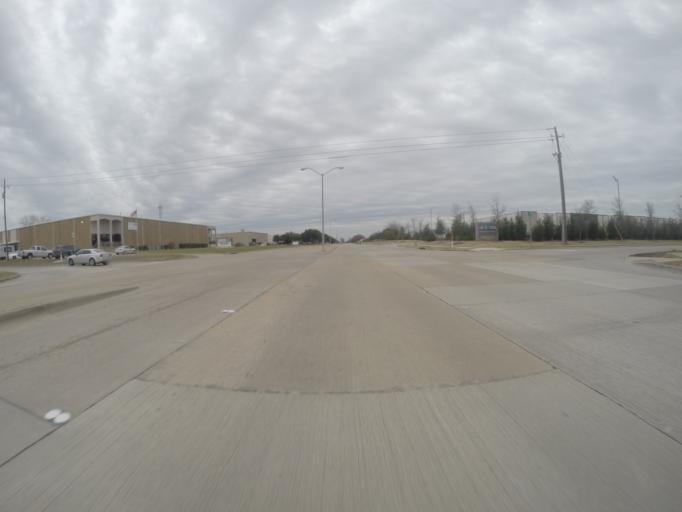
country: US
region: Texas
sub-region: Collin County
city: Saint Paul
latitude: 33.0368
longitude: -96.5607
